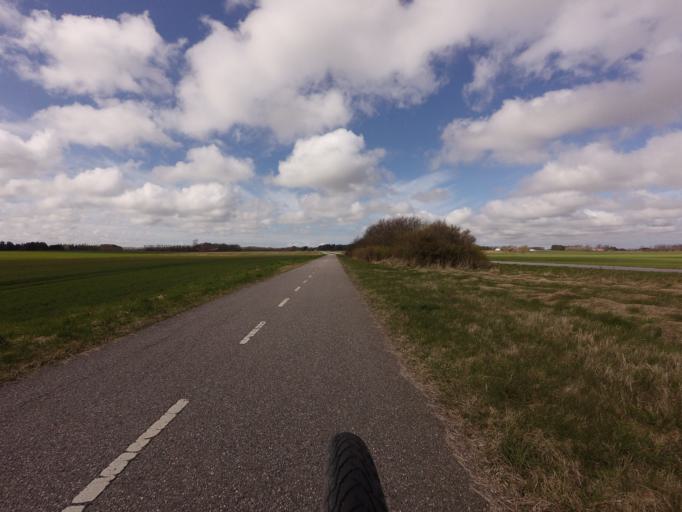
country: DK
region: North Denmark
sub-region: Hjorring Kommune
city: Vra
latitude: 57.3536
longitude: 9.8976
